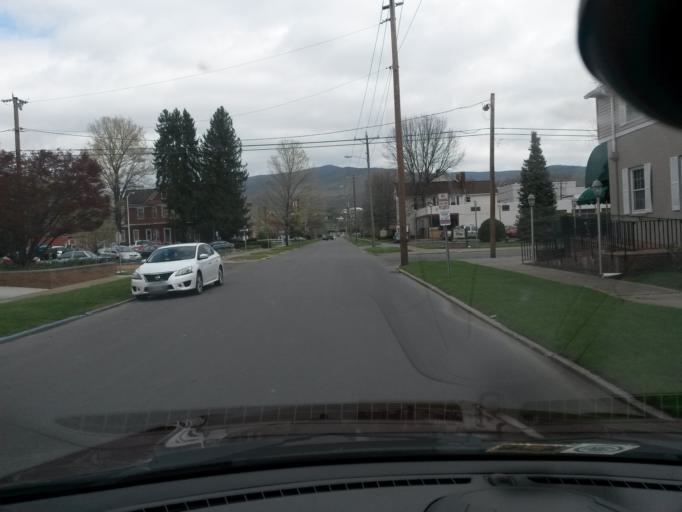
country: US
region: Virginia
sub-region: City of Covington
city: Covington
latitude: 37.7919
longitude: -79.9981
